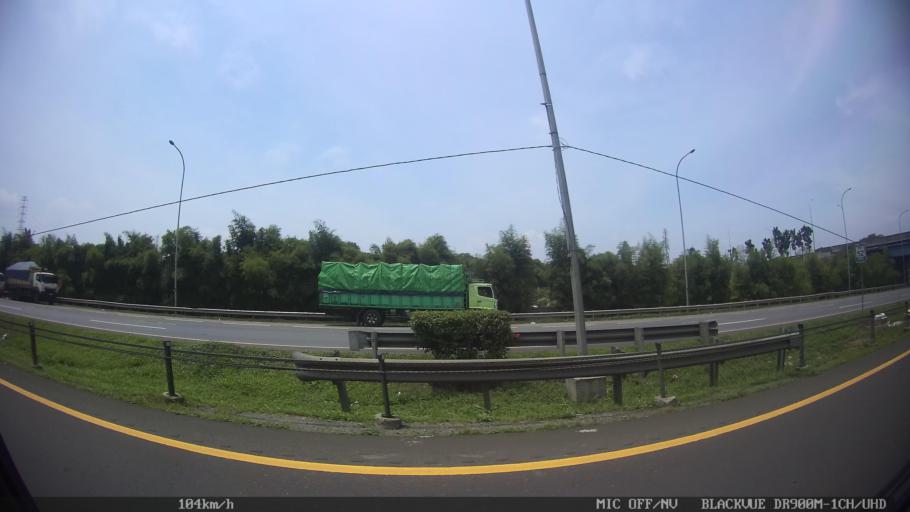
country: ID
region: West Java
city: Kresek
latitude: -6.1722
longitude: 106.3463
